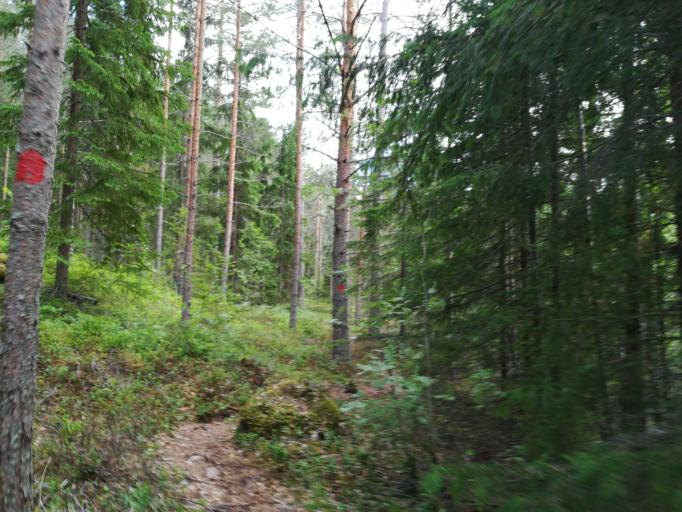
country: FI
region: South Karelia
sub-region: Lappeenranta
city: Savitaipale
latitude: 61.3055
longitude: 27.6145
